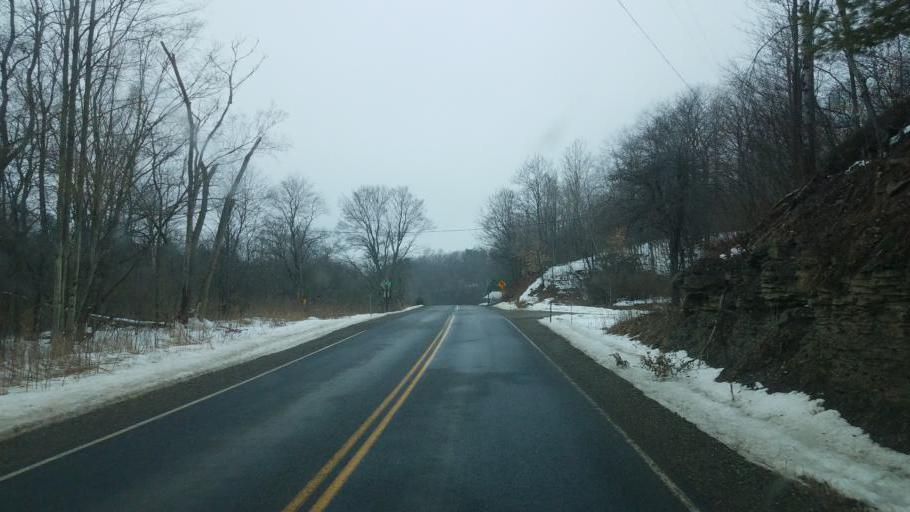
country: US
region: New York
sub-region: Allegany County
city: Andover
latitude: 42.0270
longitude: -77.7331
